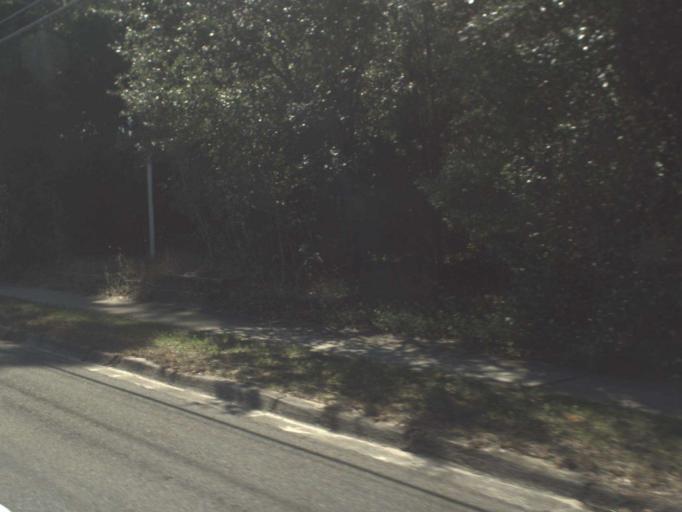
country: US
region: Florida
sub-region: Escambia County
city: Bellview
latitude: 30.4664
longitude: -87.3037
